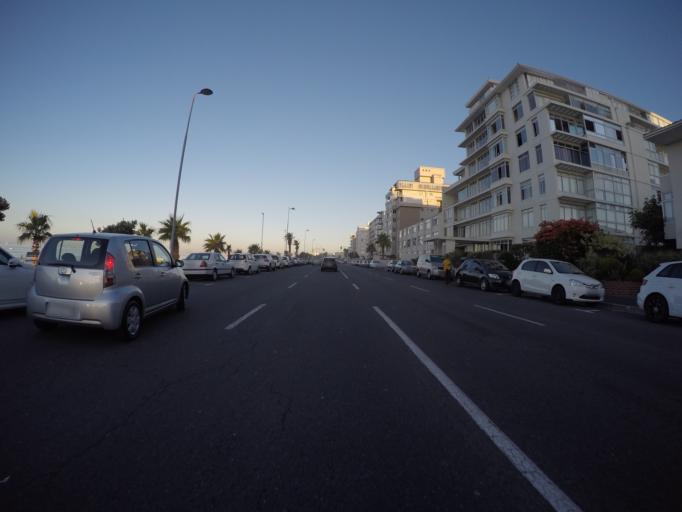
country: ZA
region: Western Cape
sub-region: City of Cape Town
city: Cape Town
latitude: -33.8998
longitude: 18.4068
